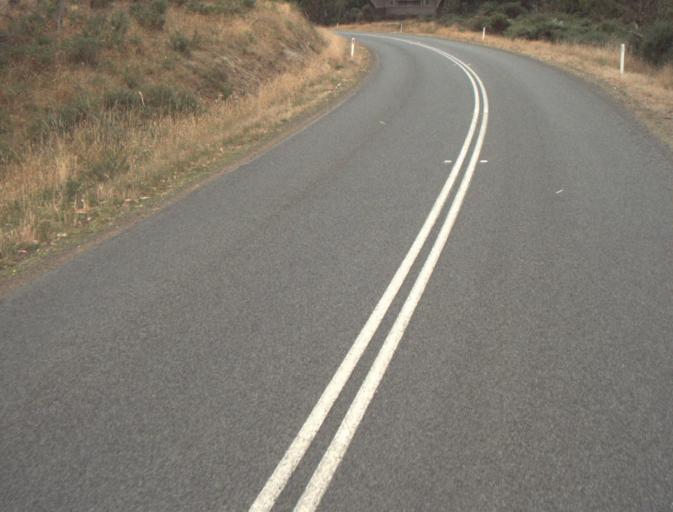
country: AU
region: Tasmania
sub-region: Northern Midlands
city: Evandale
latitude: -41.4927
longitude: 147.5007
